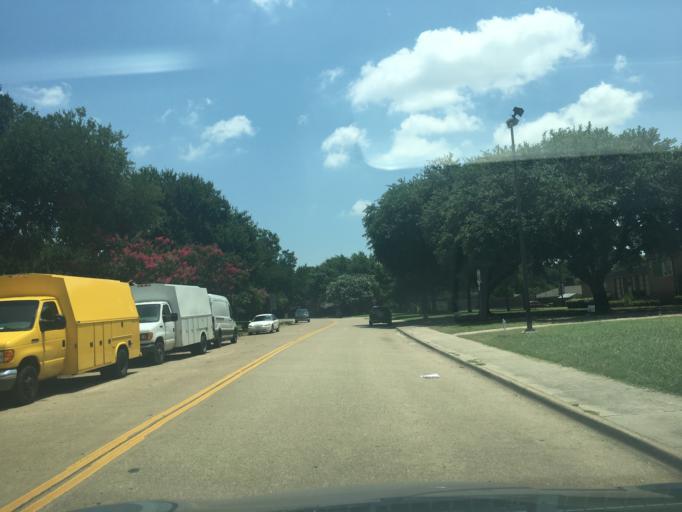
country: US
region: Texas
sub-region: Dallas County
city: Addison
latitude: 32.9178
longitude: -96.8453
